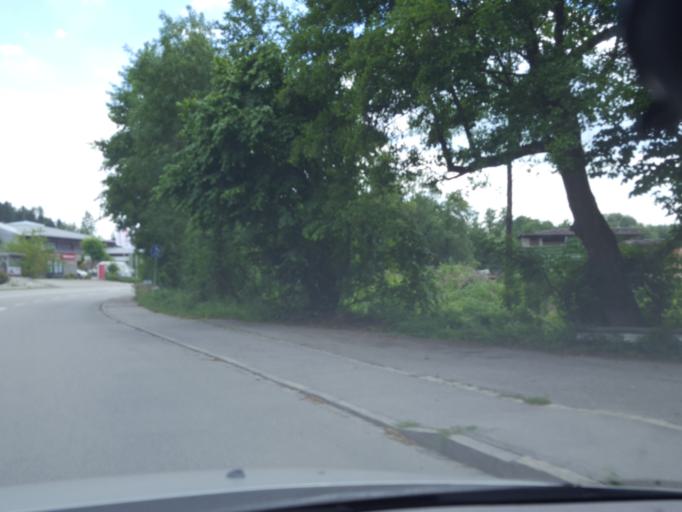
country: DE
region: Bavaria
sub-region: Lower Bavaria
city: Vilsbiburg
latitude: 48.4444
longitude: 12.3545
